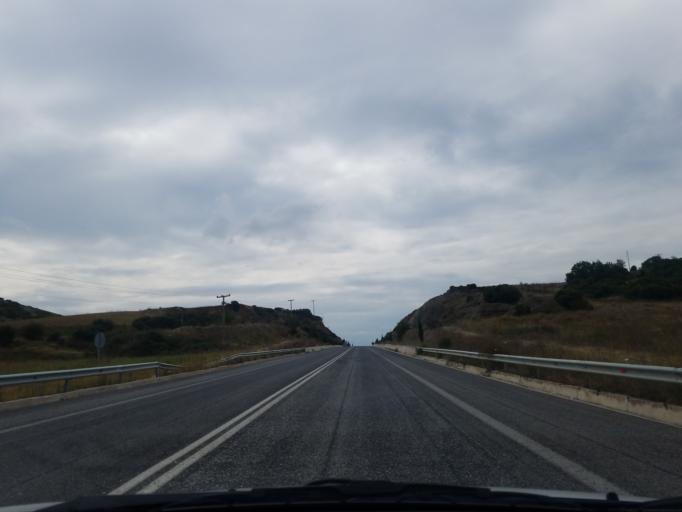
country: GR
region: Central Greece
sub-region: Nomos Fthiotidos
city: Domokos
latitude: 39.1071
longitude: 22.3071
